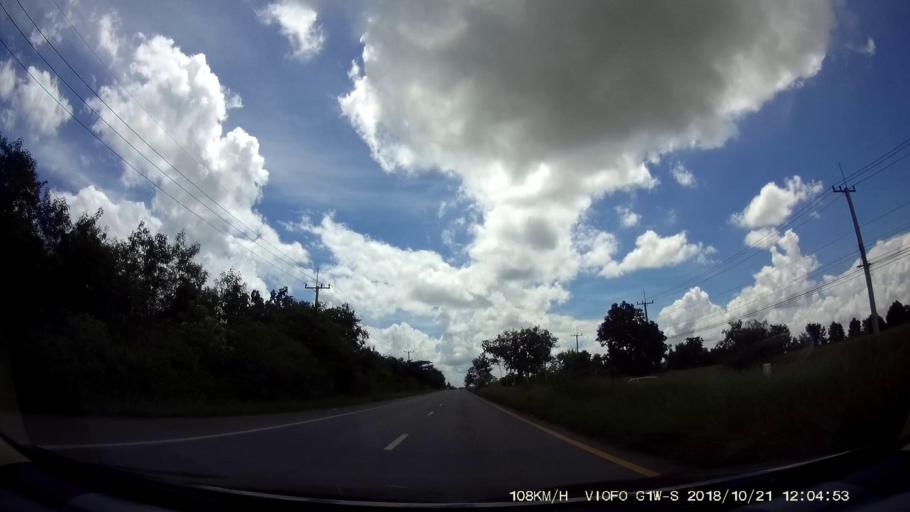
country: TH
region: Chaiyaphum
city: Chatturat
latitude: 15.4876
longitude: 101.8222
